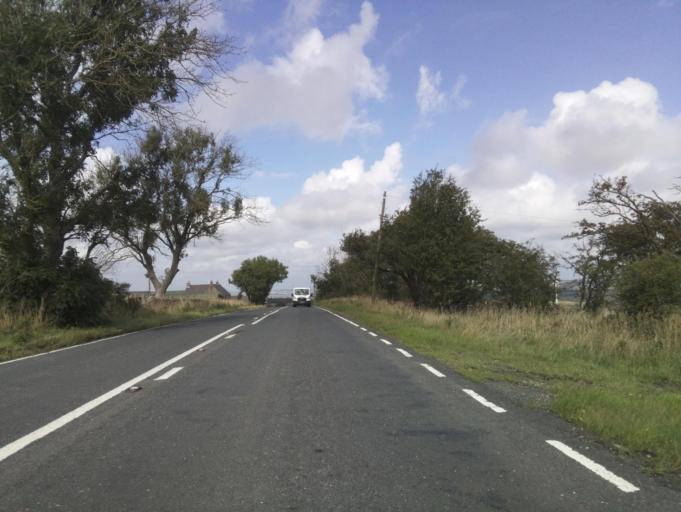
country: GB
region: England
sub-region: County Durham
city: Castleside
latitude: 54.8157
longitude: -1.8628
